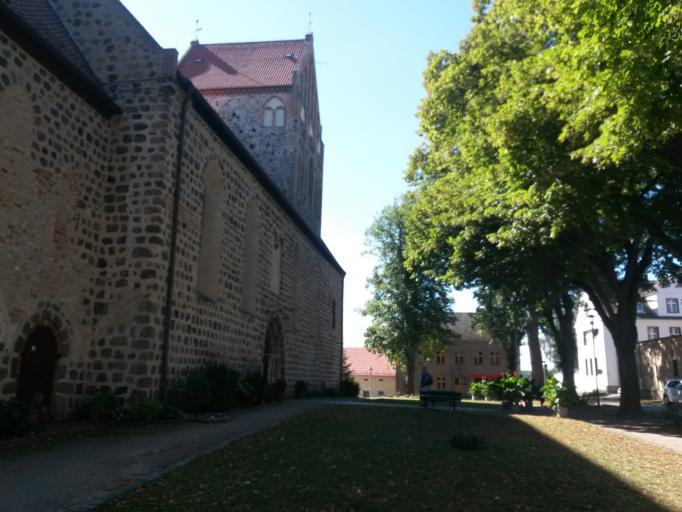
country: DE
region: Brandenburg
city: Lychen
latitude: 53.2091
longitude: 13.3159
